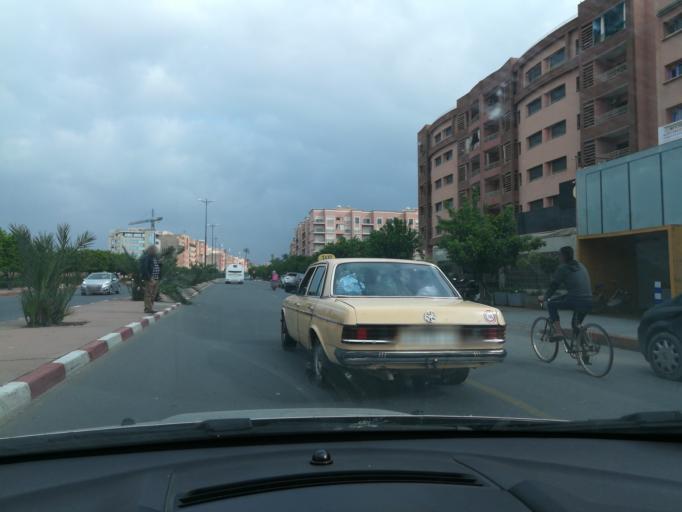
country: MA
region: Marrakech-Tensift-Al Haouz
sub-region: Marrakech
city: Marrakesh
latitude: 31.6474
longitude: -8.0121
